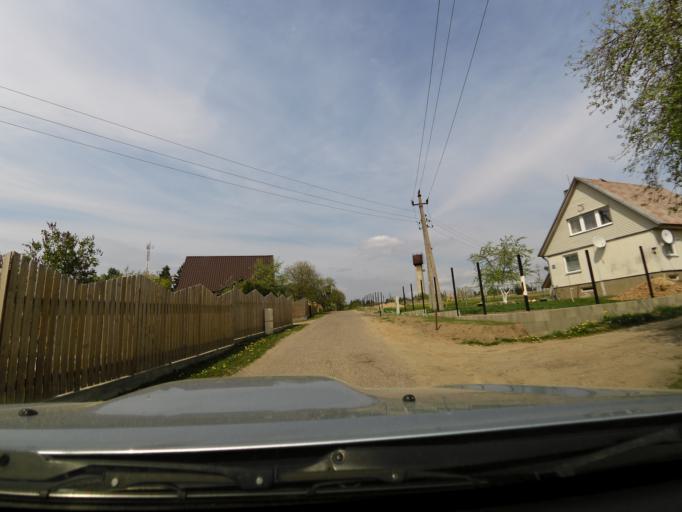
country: LT
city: Salcininkai
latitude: 54.4368
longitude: 25.3018
